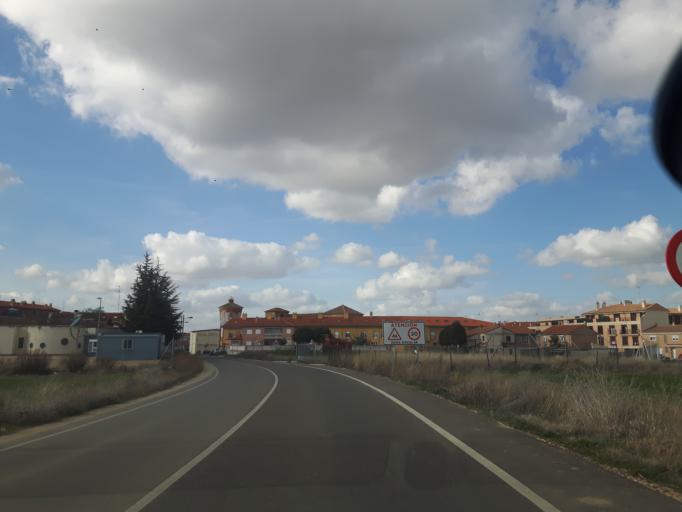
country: ES
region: Castille and Leon
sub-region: Provincia de Salamanca
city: Castellanos de Moriscos
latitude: 41.0166
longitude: -5.5885
